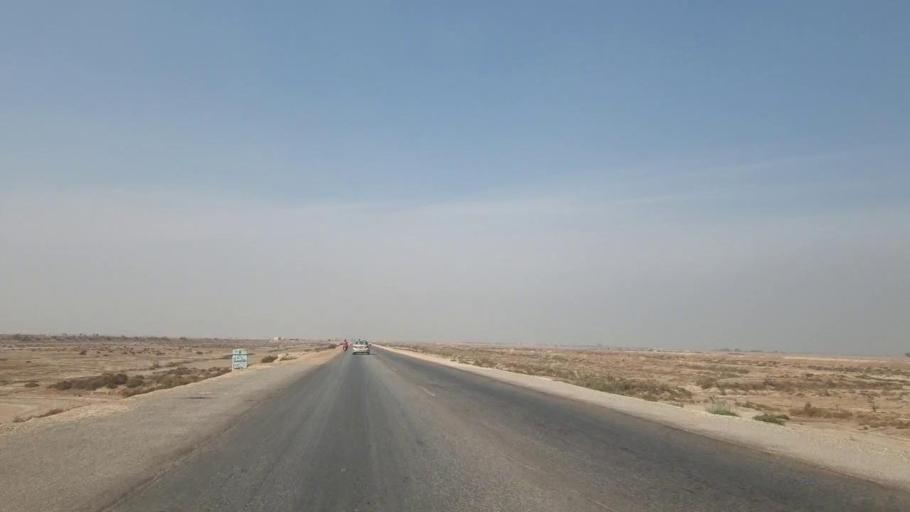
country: PK
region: Sindh
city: Hala
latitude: 25.8830
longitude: 68.2460
